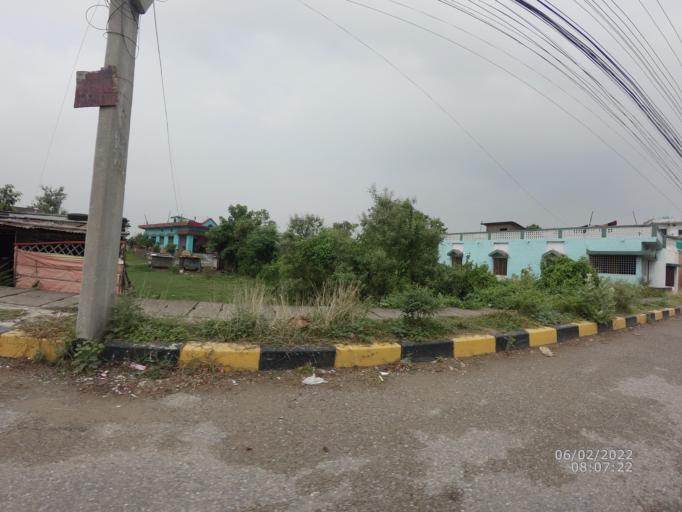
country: NP
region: Western Region
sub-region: Lumbini Zone
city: Bhairahawa
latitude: 27.4828
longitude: 83.4630
